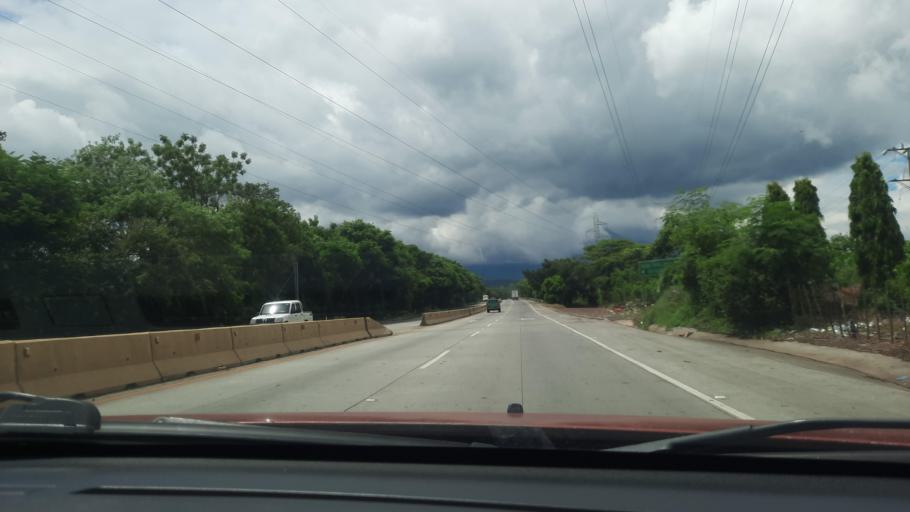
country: SV
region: Sonsonate
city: Sonsonate
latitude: 13.7183
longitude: -89.7078
